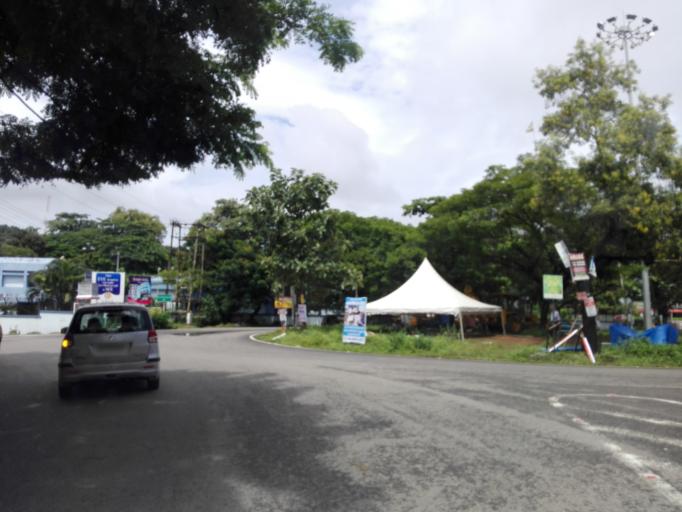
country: IN
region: Kerala
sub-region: Ernakulam
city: Elur
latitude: 10.0209
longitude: 76.3348
